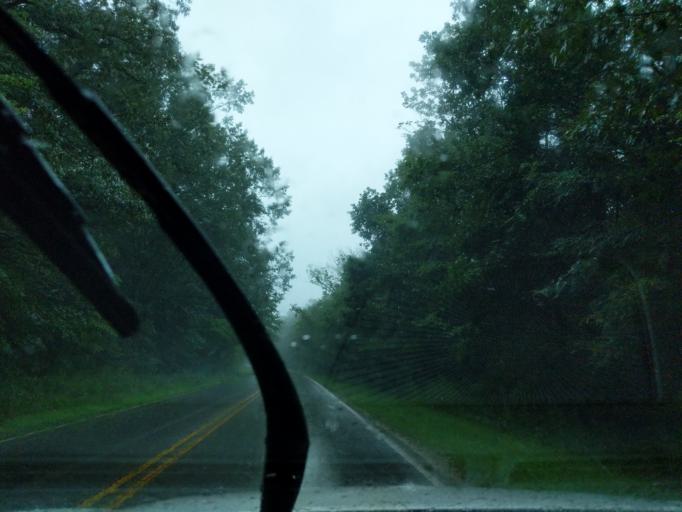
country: US
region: Kentucky
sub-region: Barren County
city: Cave City
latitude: 37.1448
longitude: -86.0883
